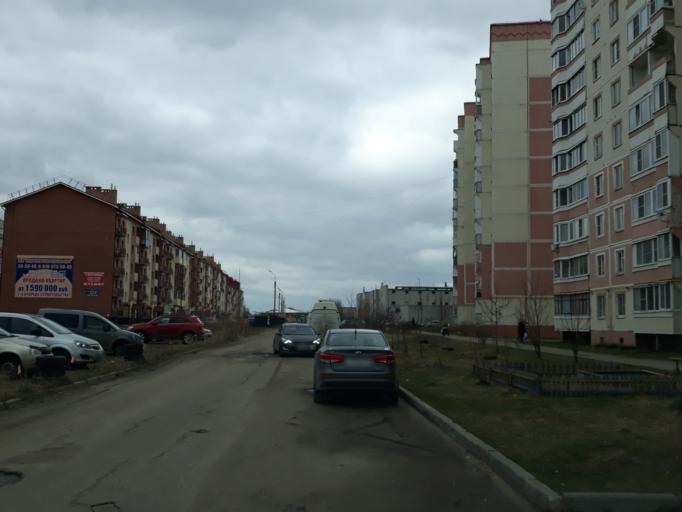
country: RU
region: Jaroslavl
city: Yaroslavl
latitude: 57.6496
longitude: 39.9685
